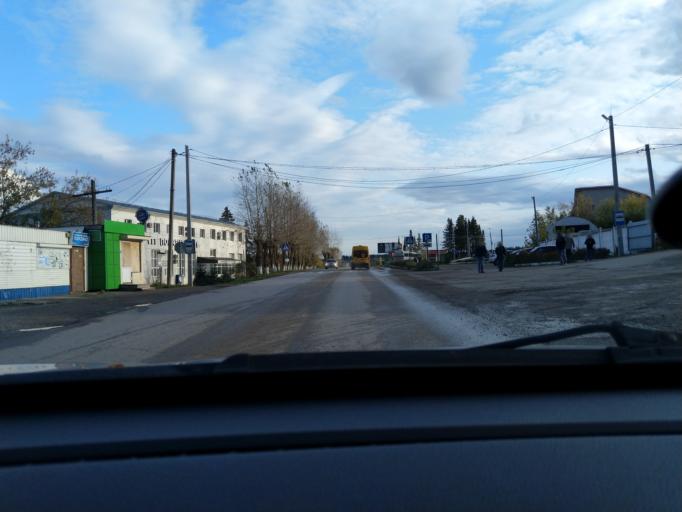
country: RU
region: Perm
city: Polazna
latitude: 58.2846
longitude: 56.4106
